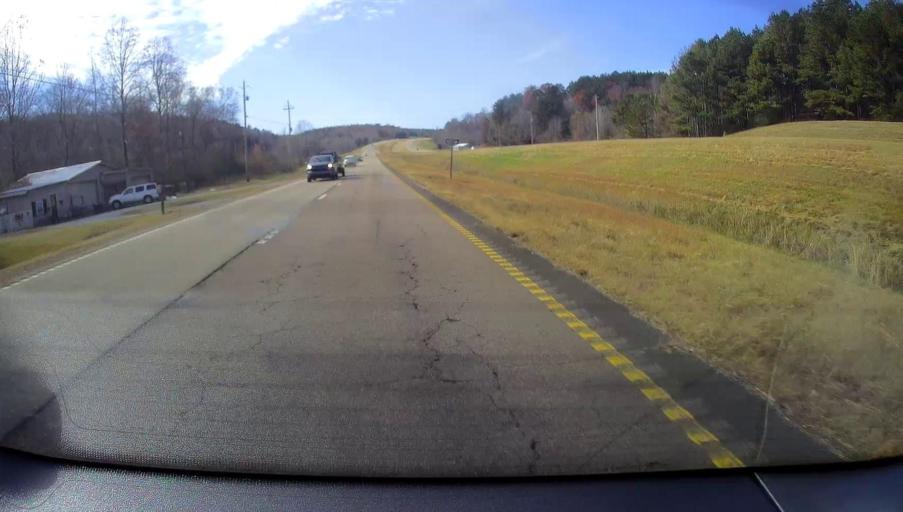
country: US
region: Mississippi
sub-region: Alcorn County
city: Corinth
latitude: 34.9337
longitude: -88.7494
